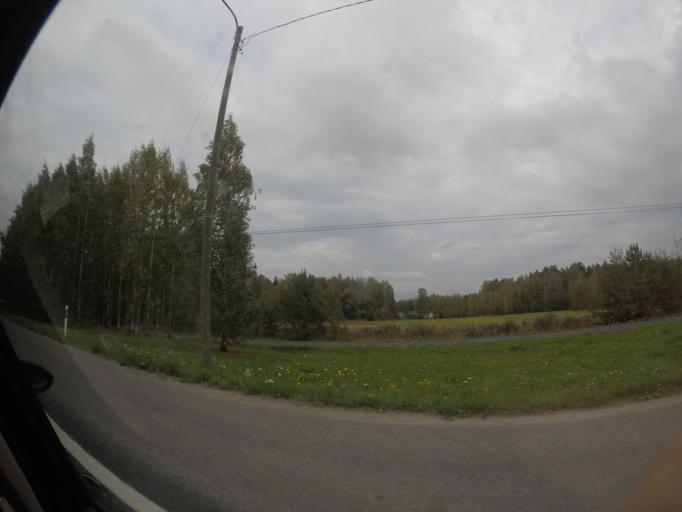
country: FI
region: Haeme
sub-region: Haemeenlinna
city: Haemeenlinna
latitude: 61.0258
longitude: 24.4218
